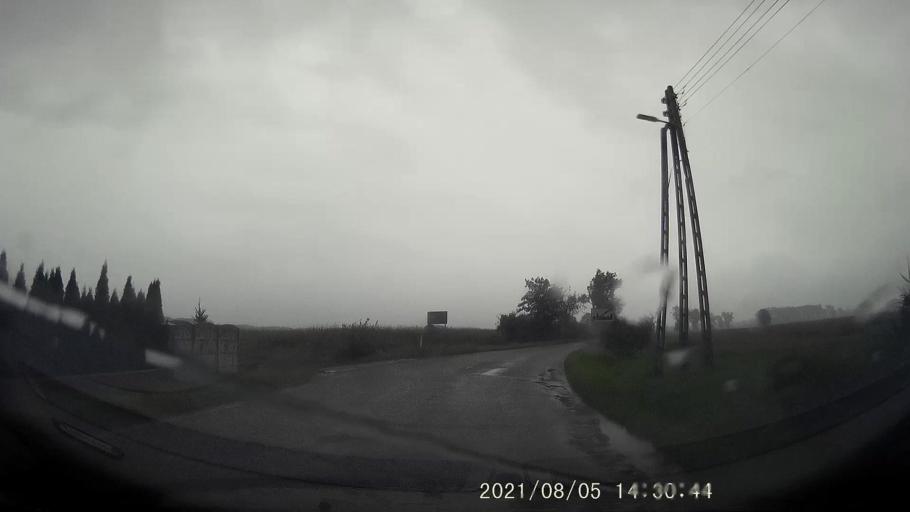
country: PL
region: Opole Voivodeship
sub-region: Powiat nyski
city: Korfantow
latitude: 50.4813
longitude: 17.5570
